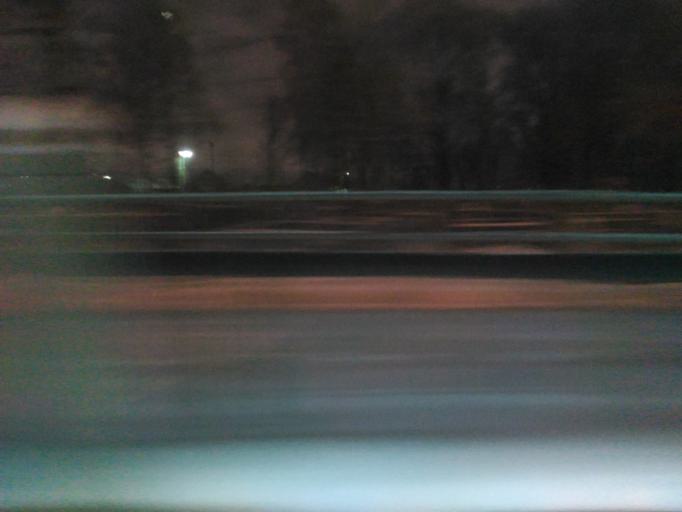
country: RU
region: Ulyanovsk
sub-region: Ulyanovskiy Rayon
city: Ulyanovsk
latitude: 54.3251
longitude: 48.3781
